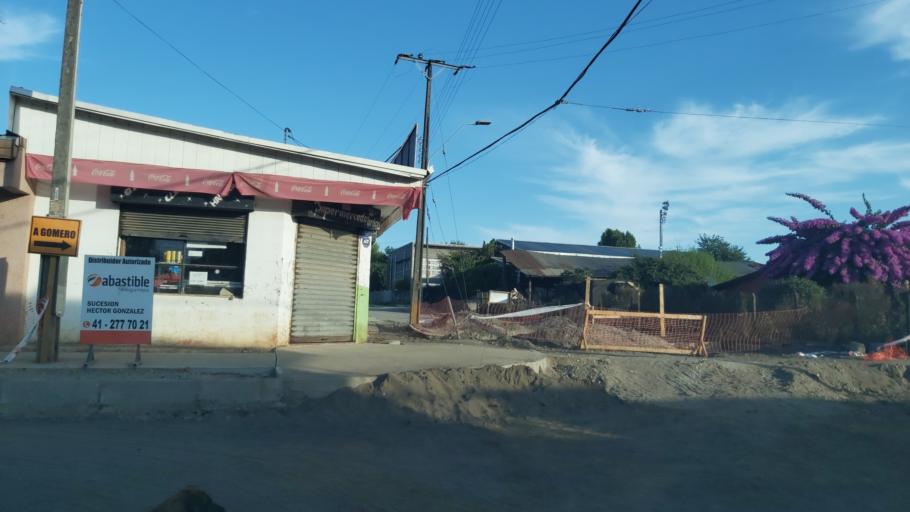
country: CL
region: Biobio
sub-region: Provincia de Biobio
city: La Laja
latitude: -37.1611
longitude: -72.9088
